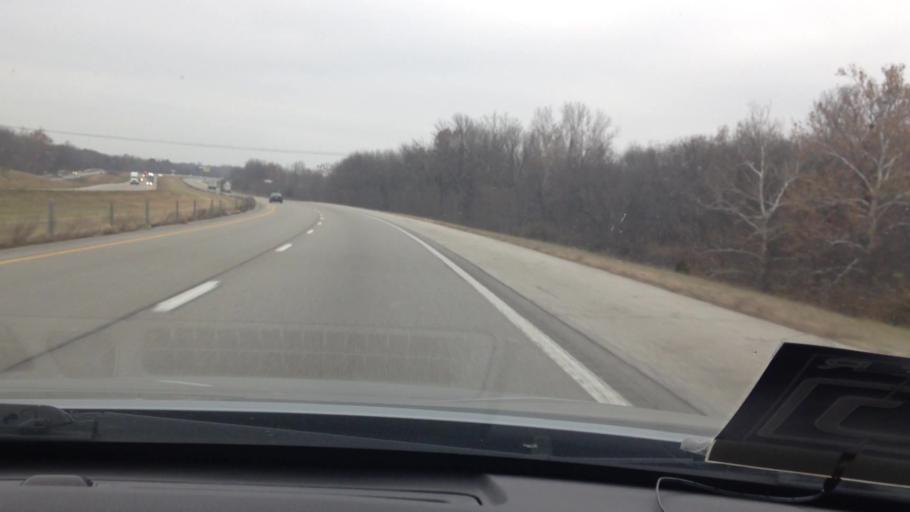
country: US
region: Missouri
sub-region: Cass County
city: Peculiar
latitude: 38.7569
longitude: -94.4825
